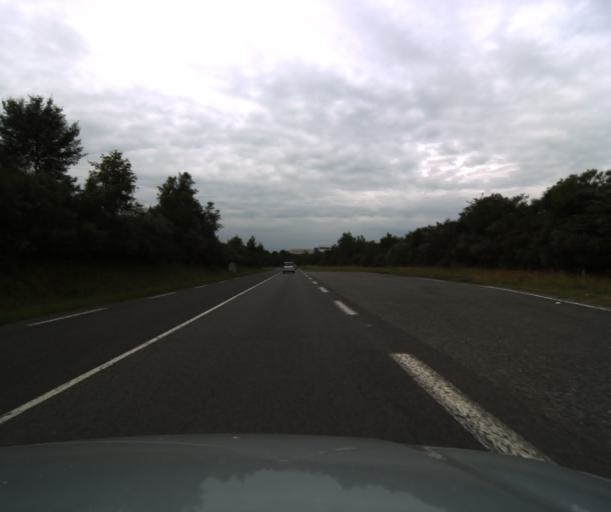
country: FR
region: Midi-Pyrenees
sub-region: Departement des Hautes-Pyrenees
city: Juillan
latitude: 43.1900
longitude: 0.0100
